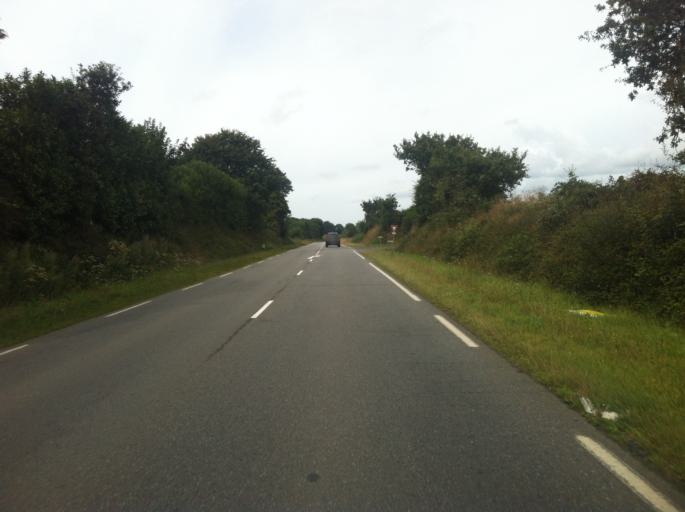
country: FR
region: Brittany
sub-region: Departement du Finistere
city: Gouesnou
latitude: 48.4412
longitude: -4.4443
